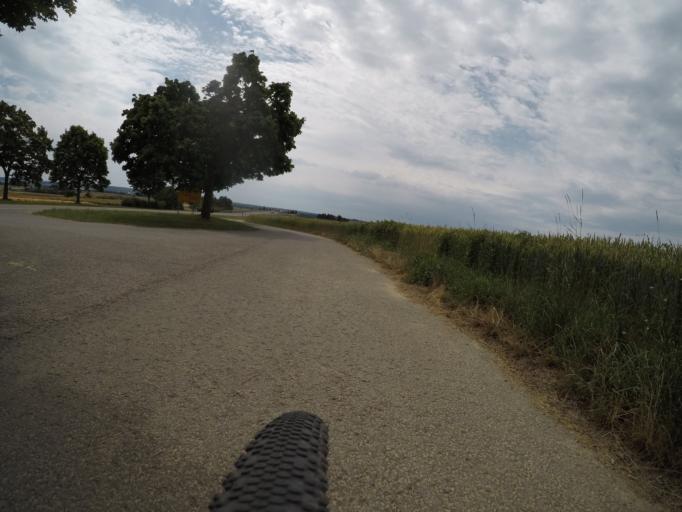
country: DE
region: Baden-Wuerttemberg
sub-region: Regierungsbezirk Stuttgart
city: Magstadt
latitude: 48.7135
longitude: 8.9519
